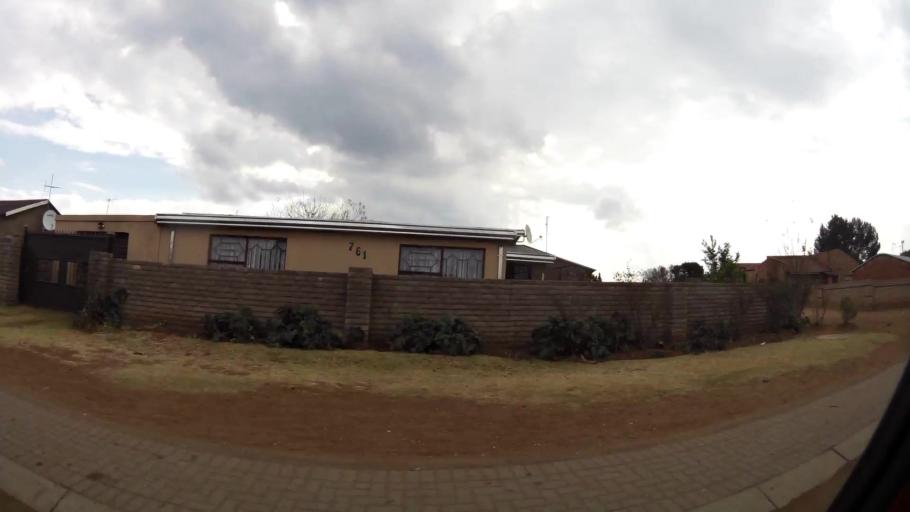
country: ZA
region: Gauteng
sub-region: Sedibeng District Municipality
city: Vanderbijlpark
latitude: -26.6642
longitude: 27.8505
